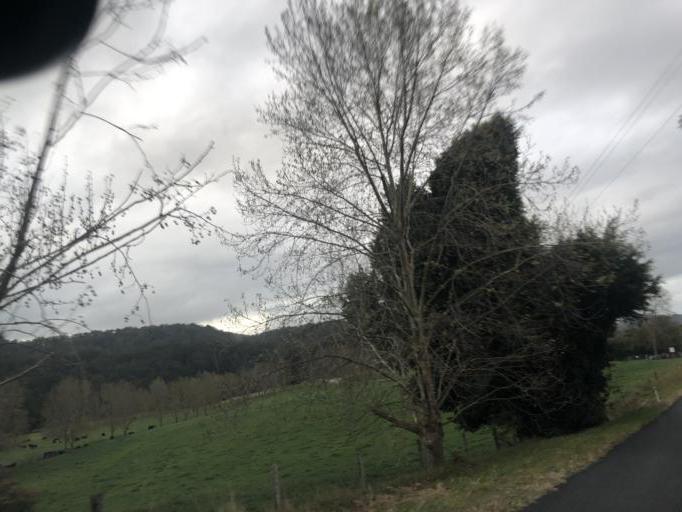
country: AU
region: New South Wales
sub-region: Coffs Harbour
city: Boambee
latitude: -30.2630
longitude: 153.0113
